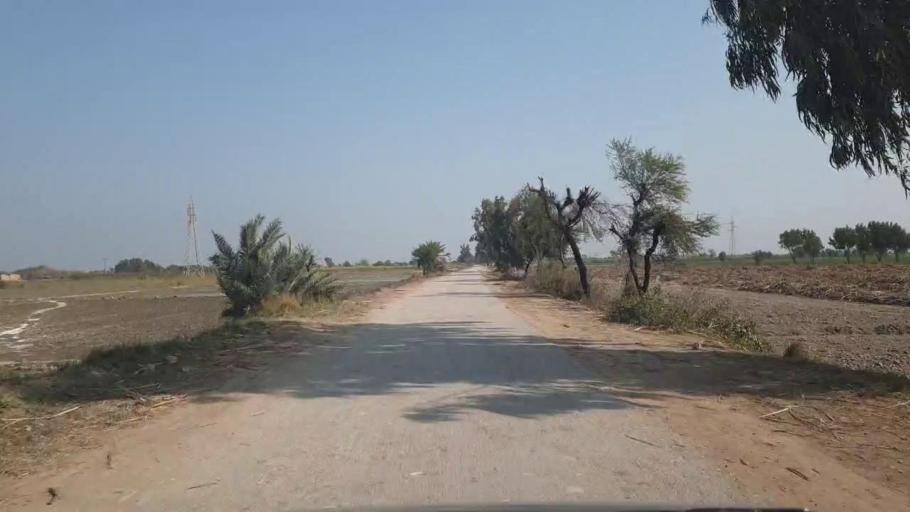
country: PK
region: Sindh
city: Tando Adam
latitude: 25.8202
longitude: 68.6407
